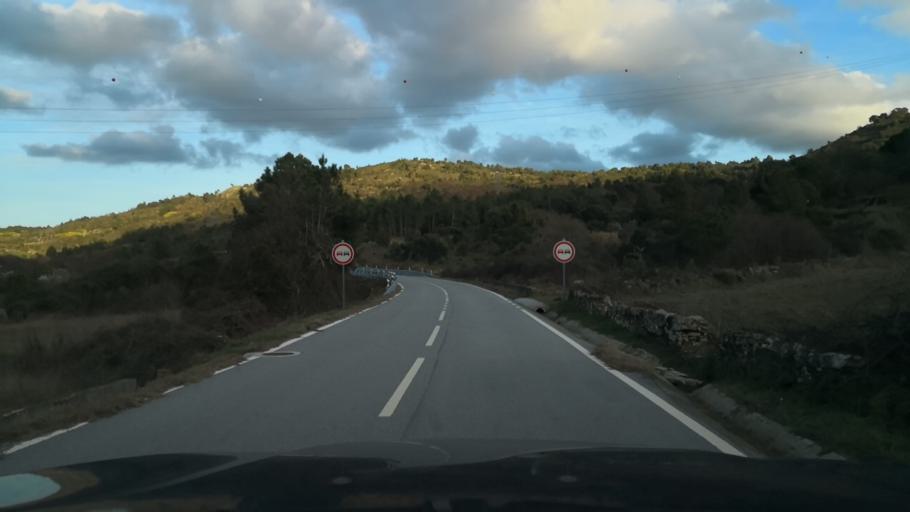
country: PT
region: Braganca
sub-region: Carrazeda de Ansiaes
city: Carrazeda de Anciaes
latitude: 41.2015
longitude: -7.3507
